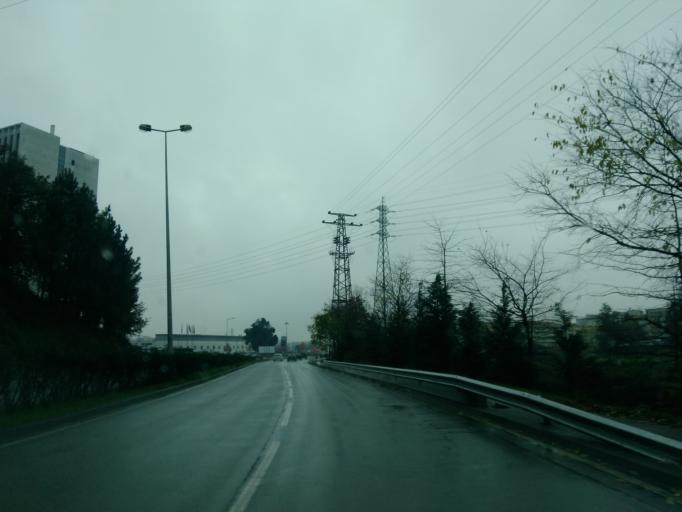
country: PT
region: Braga
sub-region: Braga
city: Braga
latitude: 41.5580
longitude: -8.3941
